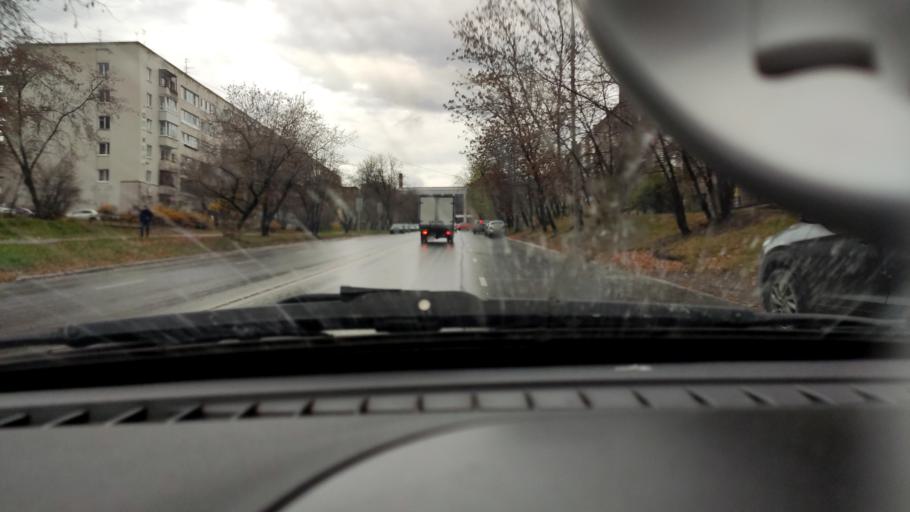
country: RU
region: Perm
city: Perm
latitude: 58.0095
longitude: 56.2112
